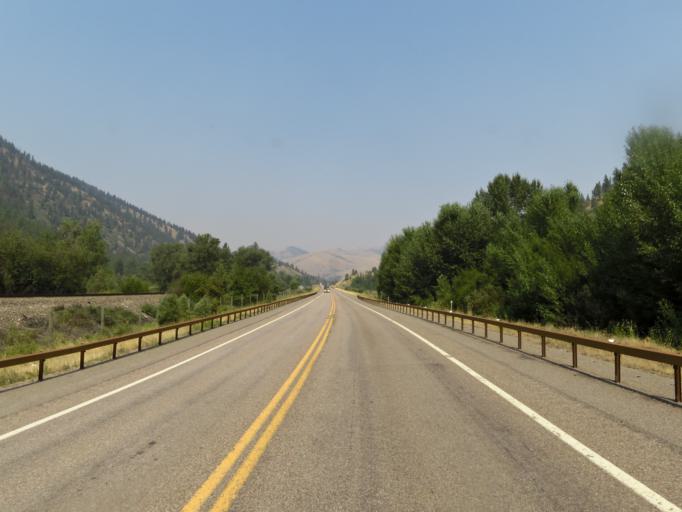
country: US
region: Montana
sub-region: Missoula County
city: Frenchtown
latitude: 47.2615
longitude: -114.1685
